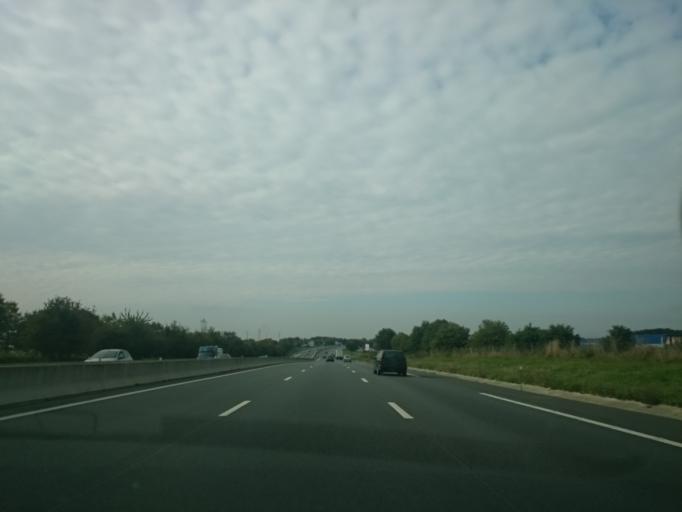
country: FR
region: Brittany
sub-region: Departement d'Ille-et-Vilaine
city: Vezin-le-Coquet
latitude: 48.1332
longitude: -1.7608
